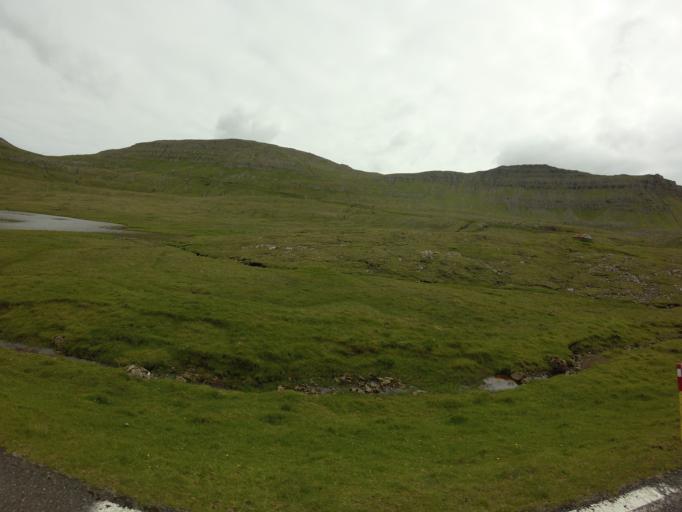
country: FO
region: Suduroy
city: Tvoroyri
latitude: 61.5174
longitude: -6.8483
